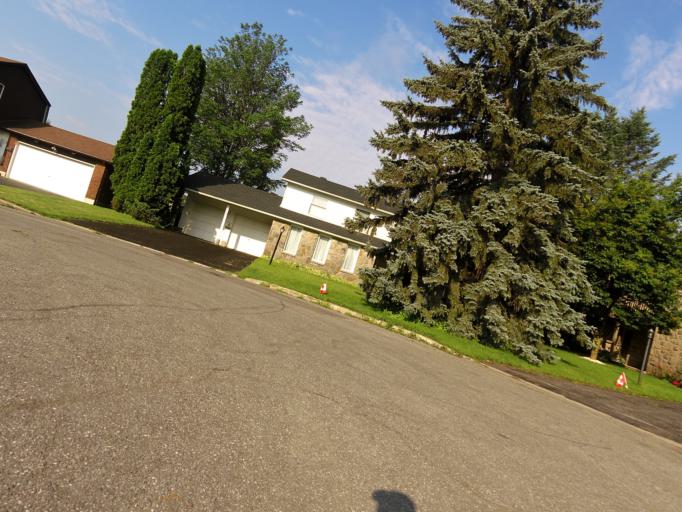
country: CA
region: Ontario
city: Bells Corners
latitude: 45.3368
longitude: -75.8044
